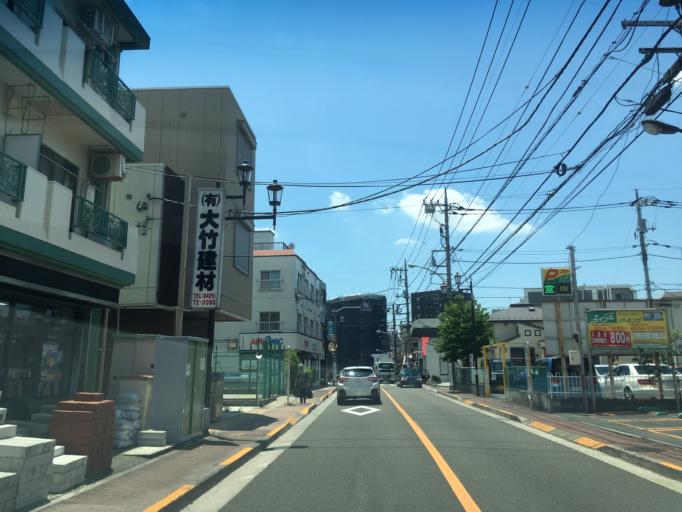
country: JP
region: Tokyo
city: Kokubunji
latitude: 35.7016
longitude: 139.4502
